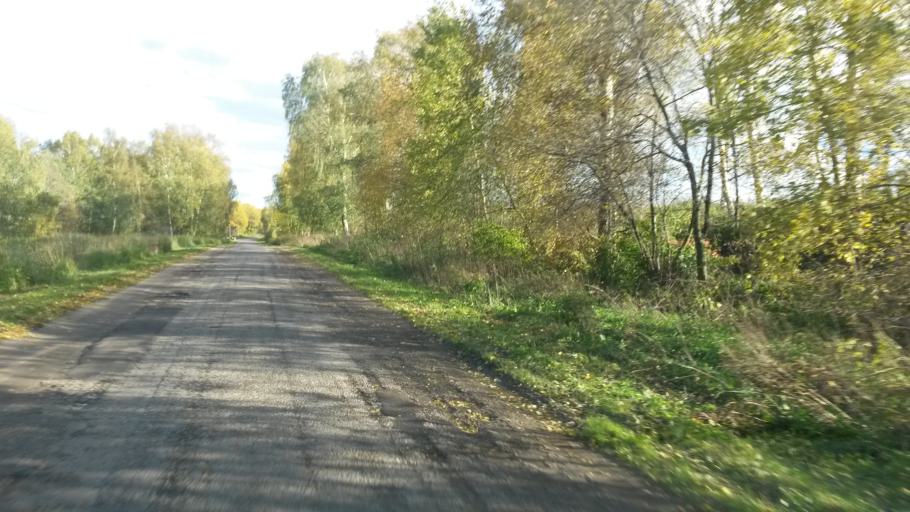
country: RU
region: Jaroslavl
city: Tunoshna
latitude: 57.5251
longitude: 40.0060
